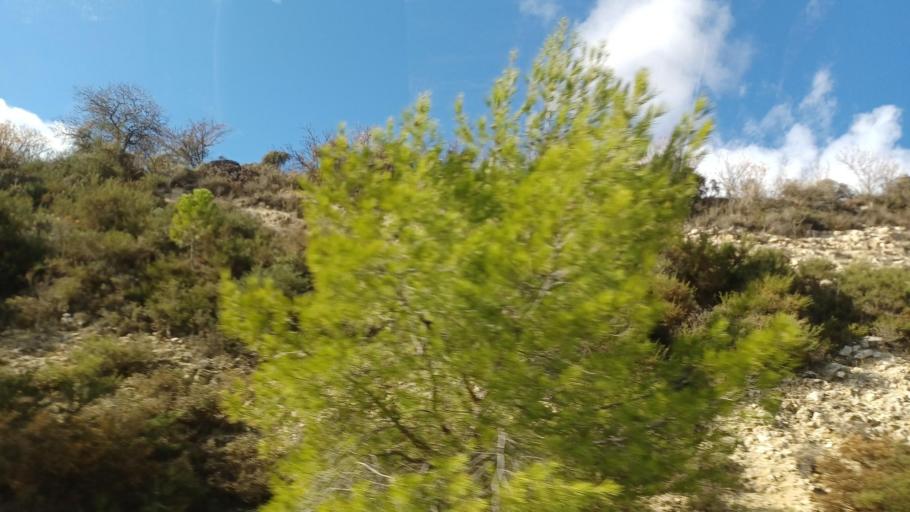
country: CY
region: Limassol
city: Pachna
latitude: 34.8478
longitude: 32.8049
